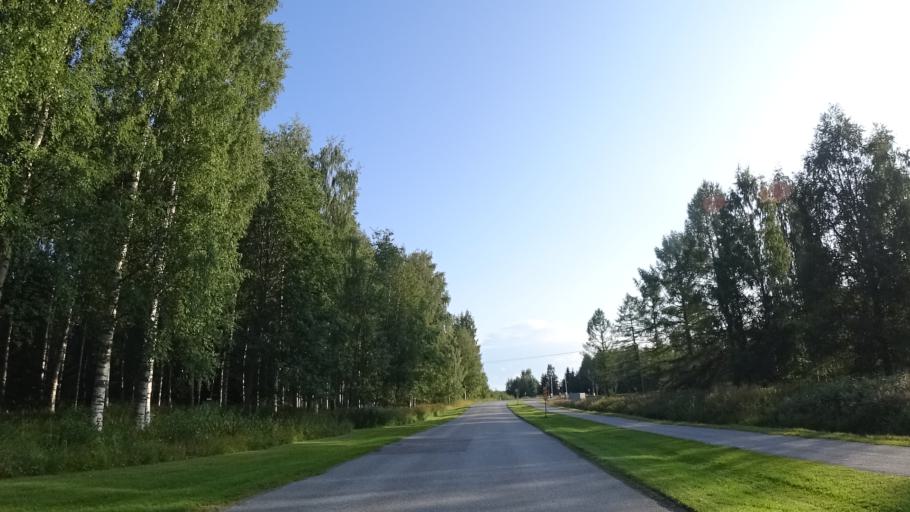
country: FI
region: North Karelia
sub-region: Pielisen Karjala
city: Lieksa
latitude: 63.3118
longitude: 30.0258
